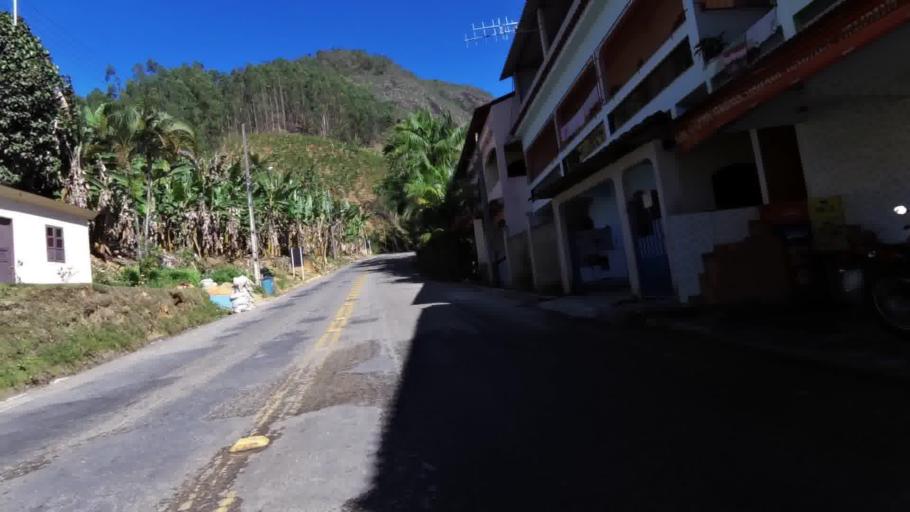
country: BR
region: Espirito Santo
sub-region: Iconha
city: Iconha
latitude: -20.7297
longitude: -40.8834
